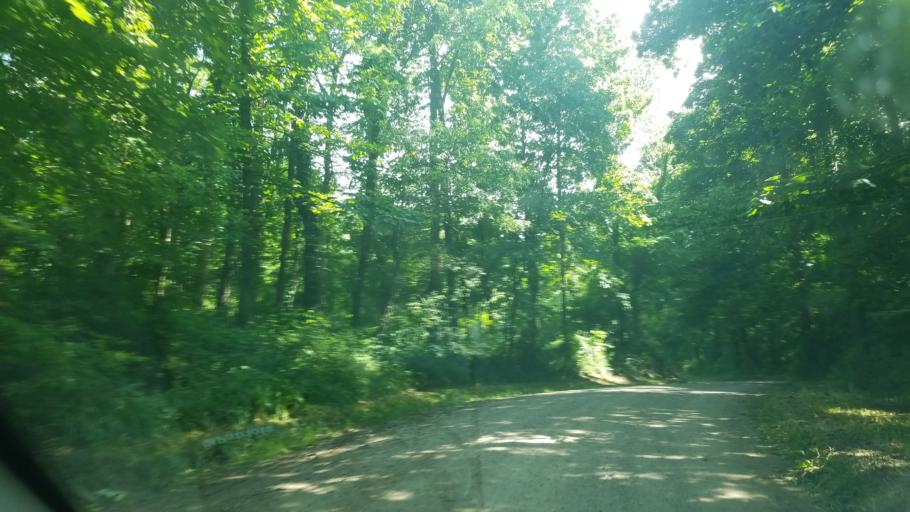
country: US
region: Ohio
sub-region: Holmes County
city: Millersburg
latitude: 40.4508
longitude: -81.9477
